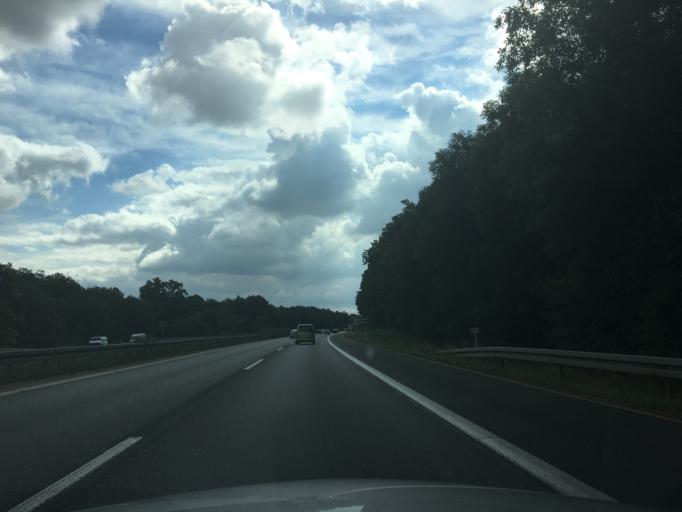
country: DE
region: Bavaria
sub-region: Regierungsbezirk Unterfranken
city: Dettelbach
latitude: 49.7889
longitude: 10.1789
